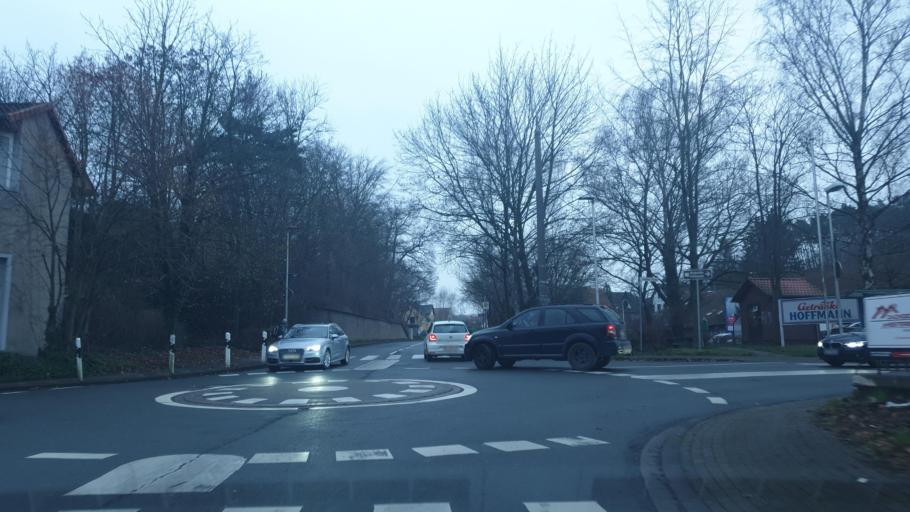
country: DE
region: North Rhine-Westphalia
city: Porta Westfalica
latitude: 52.2353
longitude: 8.9124
